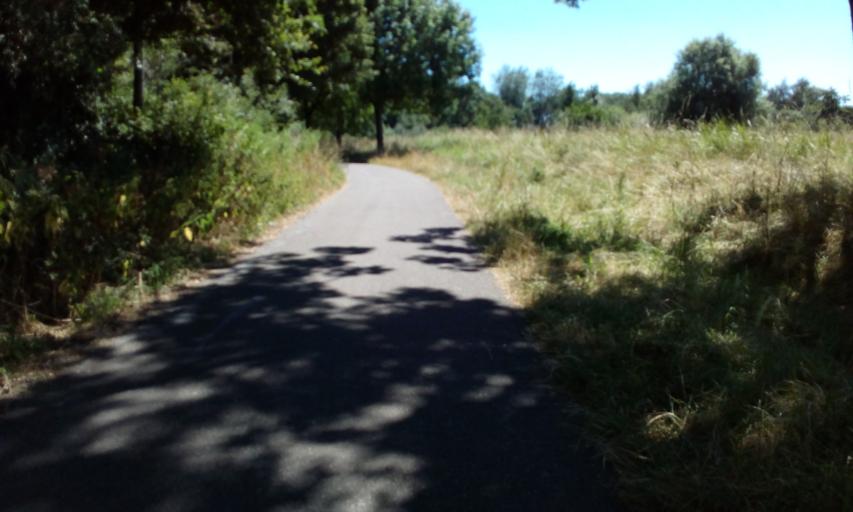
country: NL
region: South Holland
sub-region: Gemeente Leiden
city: Leiden
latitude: 52.1415
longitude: 4.5033
